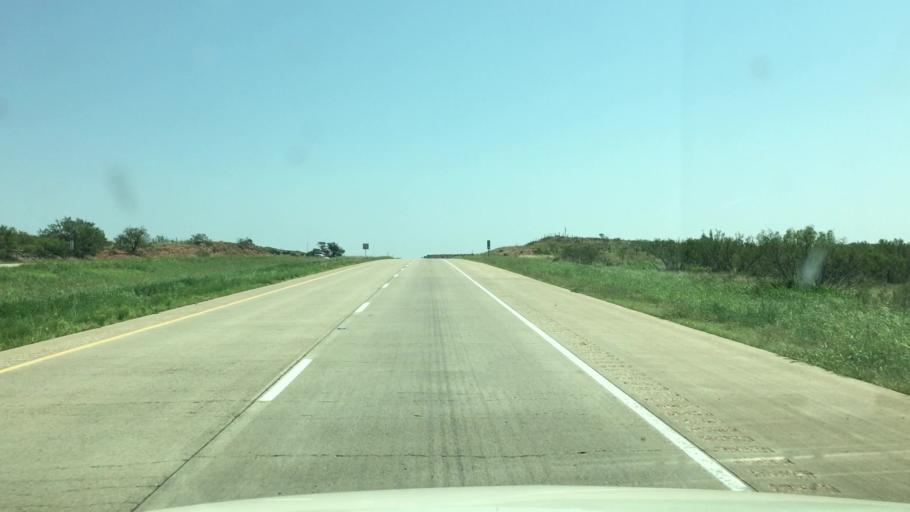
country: US
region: Texas
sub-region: Oldham County
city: Vega
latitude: 35.2448
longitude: -102.8133
